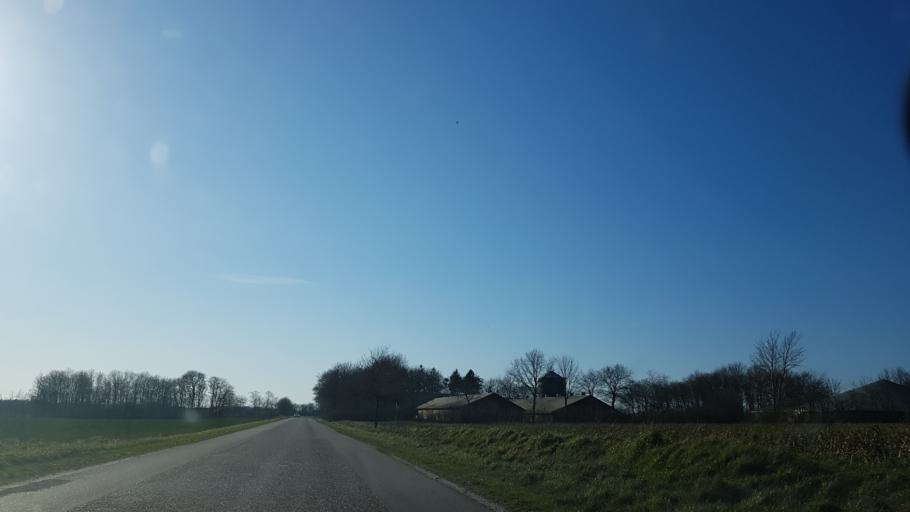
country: DK
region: South Denmark
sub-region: Vejen Kommune
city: Rodding
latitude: 55.3846
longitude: 8.9917
